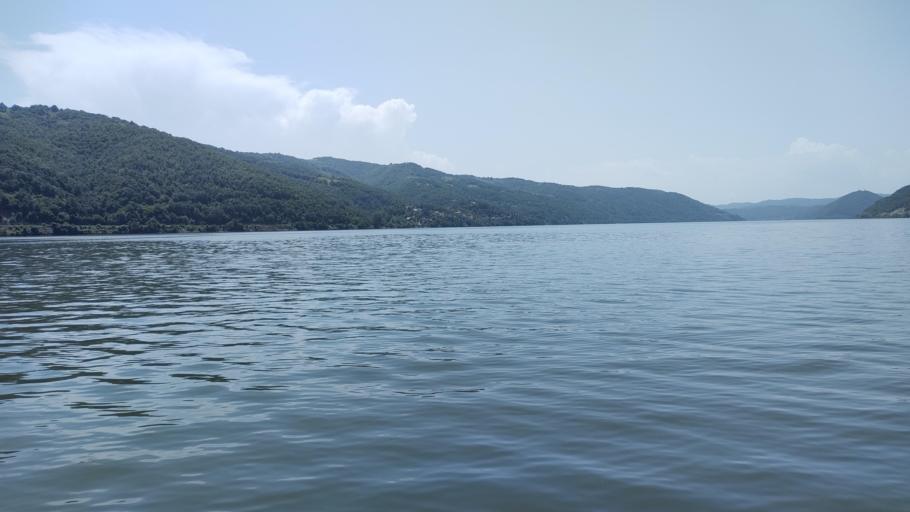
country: RO
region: Mehedinti
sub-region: Comuna Svinita
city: Svinita
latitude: 44.5167
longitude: 22.1996
